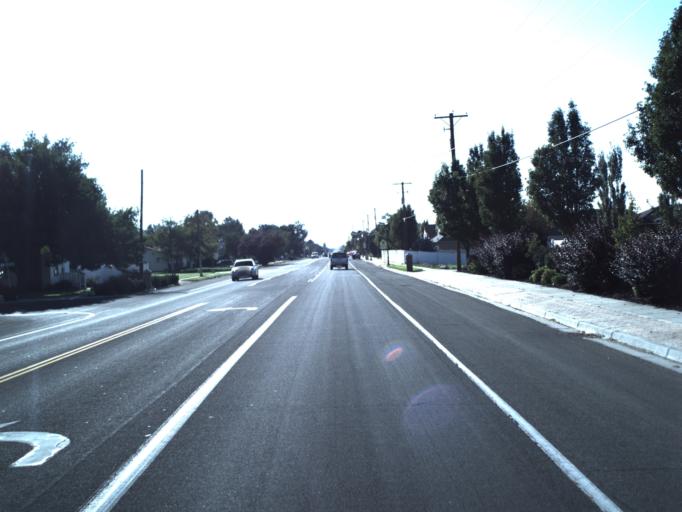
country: US
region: Utah
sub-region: Davis County
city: West Point
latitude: 41.1399
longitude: -112.0758
